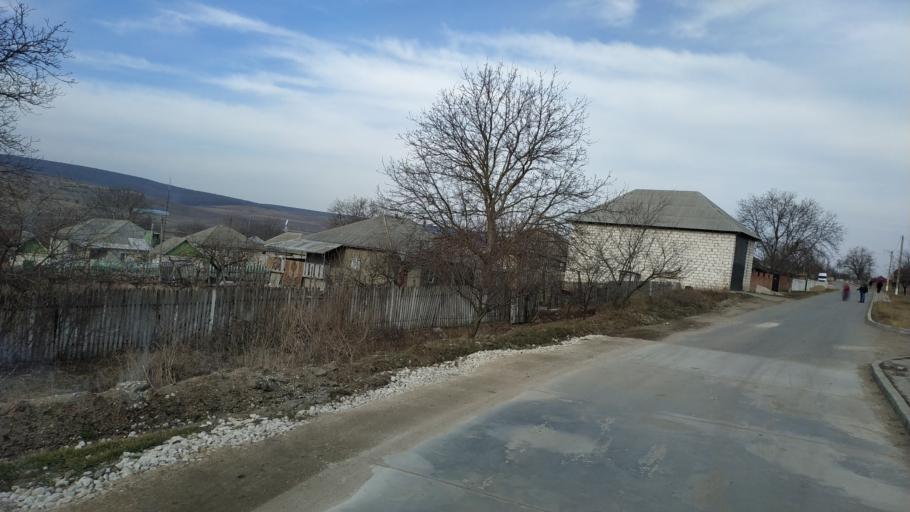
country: MD
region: Chisinau
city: Vatra
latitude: 46.9863
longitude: 28.6685
